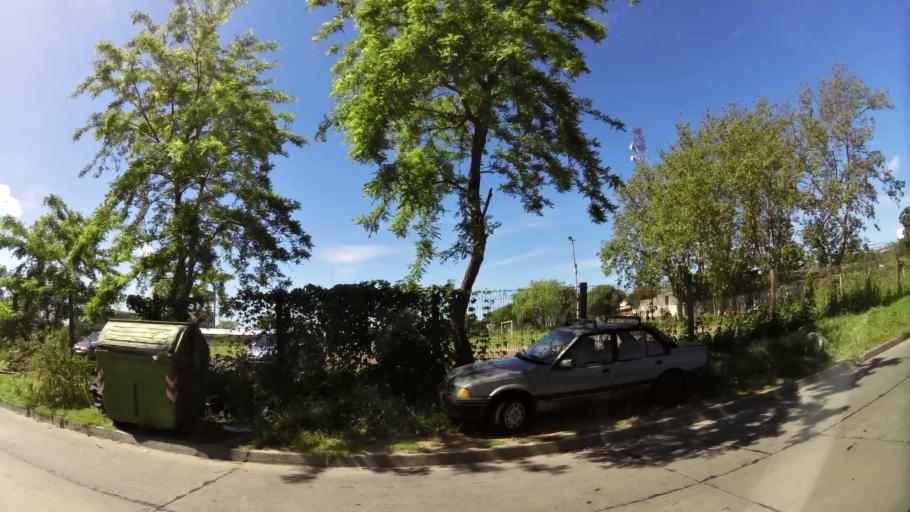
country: UY
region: Montevideo
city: Montevideo
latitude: -34.8478
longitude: -56.1324
